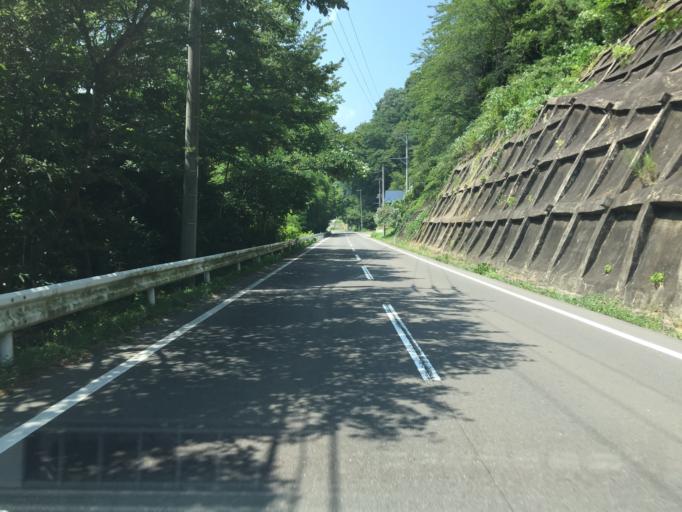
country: JP
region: Miyagi
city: Marumori
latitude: 37.9353
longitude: 140.7083
